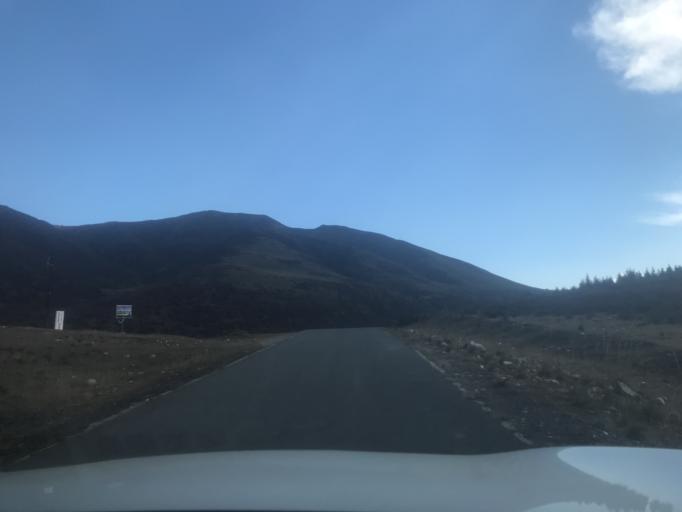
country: CN
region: Gansu Sheng
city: Gulang
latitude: 37.3690
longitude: 102.7577
